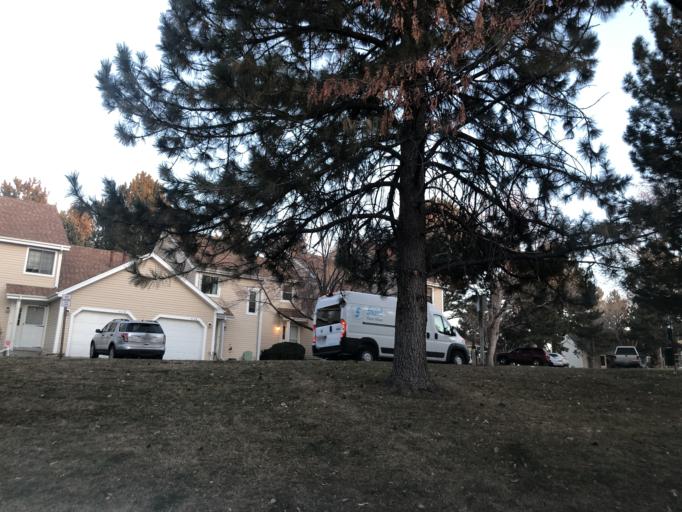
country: US
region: Colorado
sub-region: Adams County
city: Aurora
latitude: 39.7087
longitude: -104.8015
